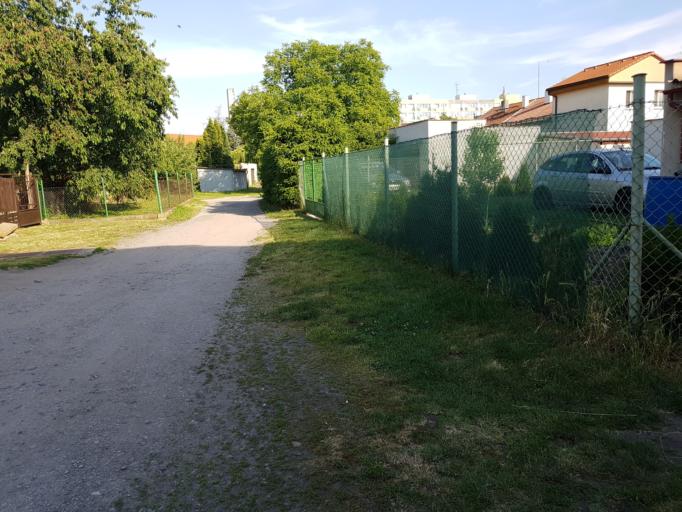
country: CZ
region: Central Bohemia
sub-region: Okres Nymburk
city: Podebrady
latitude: 50.1534
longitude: 15.1325
